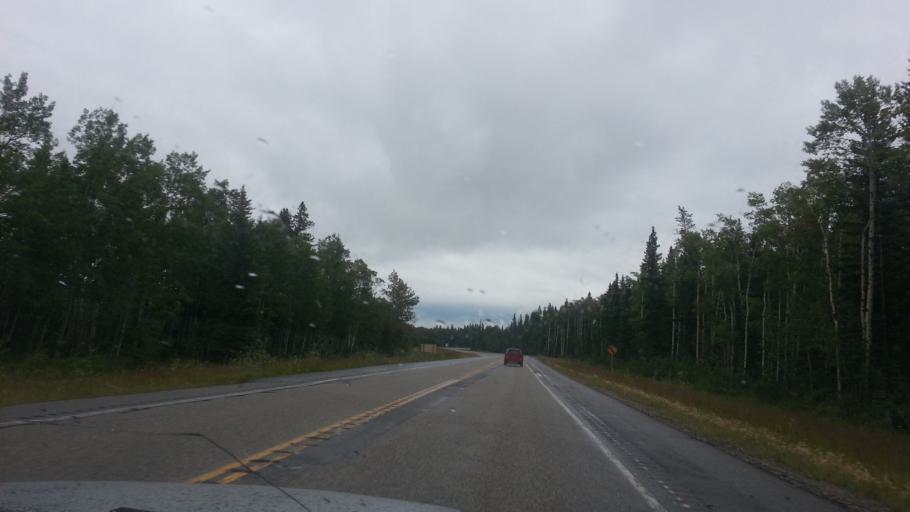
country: CA
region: Alberta
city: Cochrane
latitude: 50.9102
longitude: -114.6501
